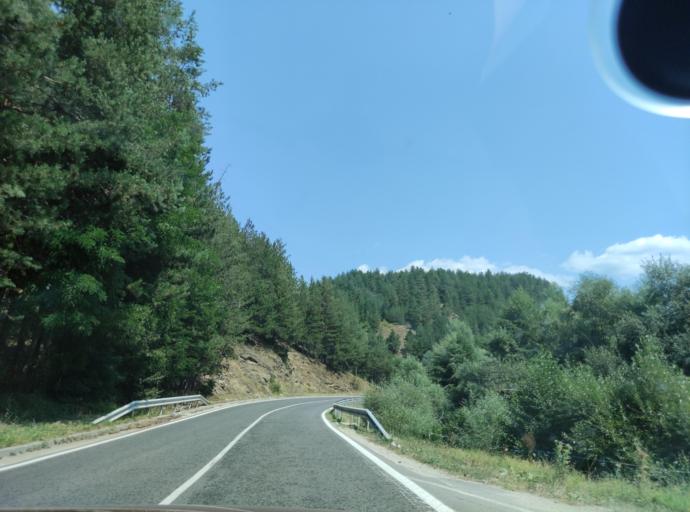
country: BG
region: Blagoevgrad
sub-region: Obshtina Razlog
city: Razlog
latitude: 41.8943
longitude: 23.5380
